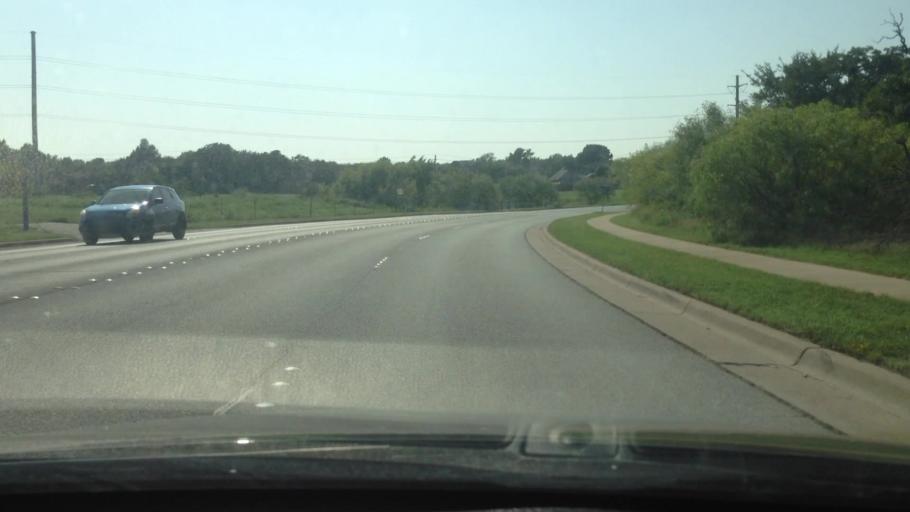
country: US
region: Texas
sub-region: Tarrant County
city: Colleyville
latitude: 32.8828
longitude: -97.1864
